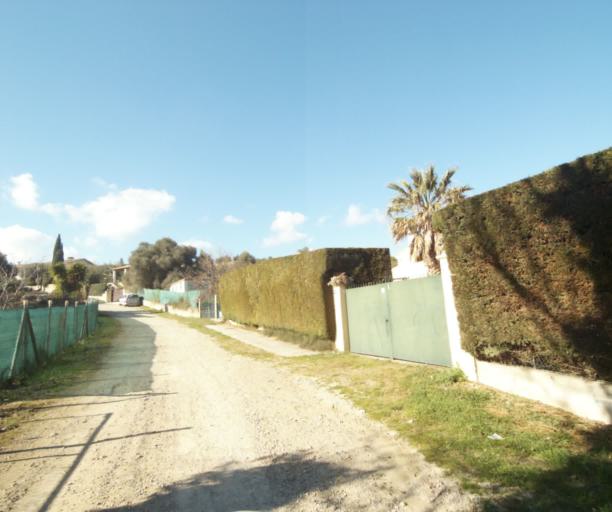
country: FR
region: Provence-Alpes-Cote d'Azur
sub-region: Departement des Alpes-Maritimes
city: Biot
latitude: 43.6162
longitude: 7.1192
